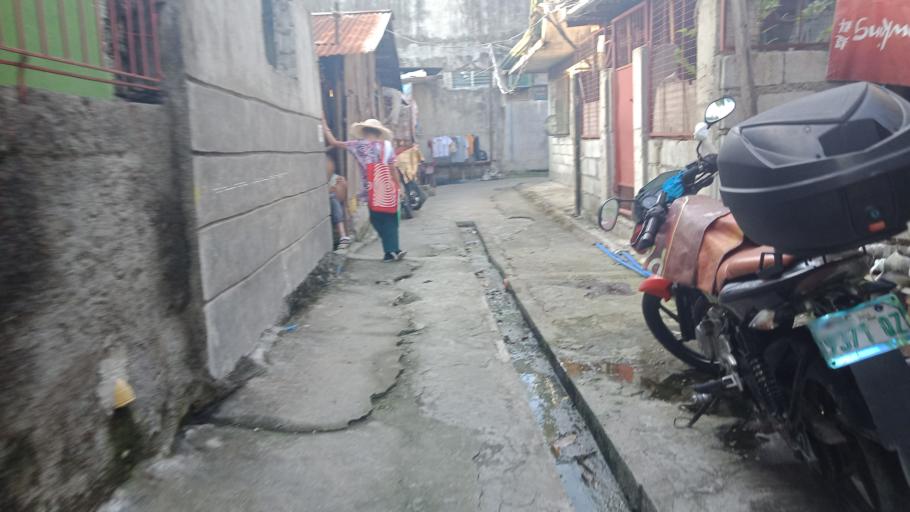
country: PH
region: Calabarzon
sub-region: Province of Rizal
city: Pateros
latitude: 14.5439
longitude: 121.0995
